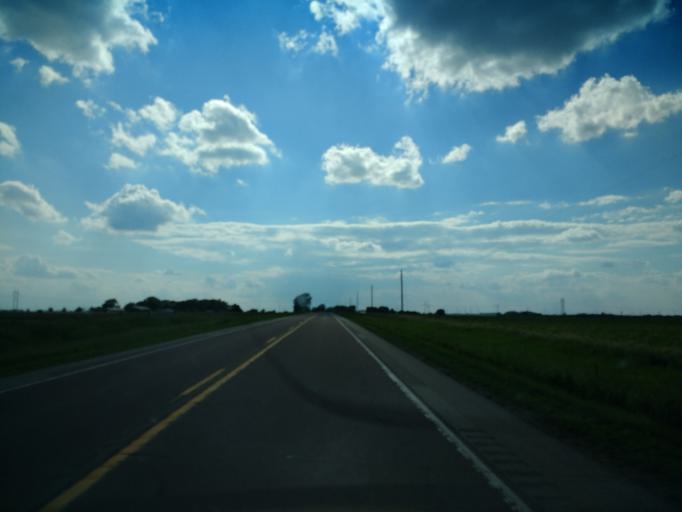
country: US
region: Iowa
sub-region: Clay County
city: Spencer
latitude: 43.1835
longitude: -95.2347
